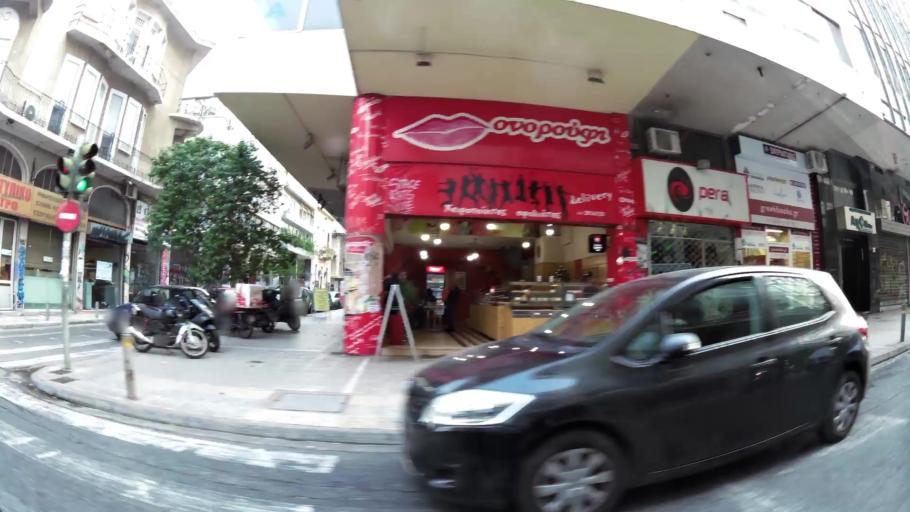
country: GR
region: Attica
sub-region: Nomarchia Athinas
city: Athens
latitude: 37.9837
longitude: 23.7340
